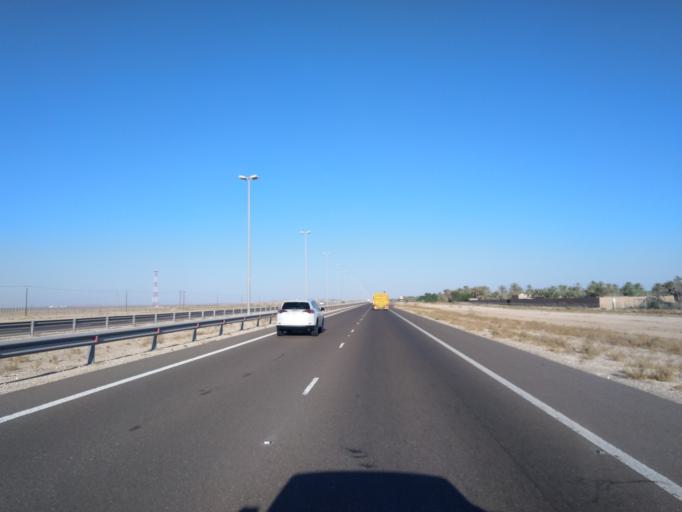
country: OM
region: Al Buraimi
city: Al Buraymi
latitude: 24.4852
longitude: 55.3879
